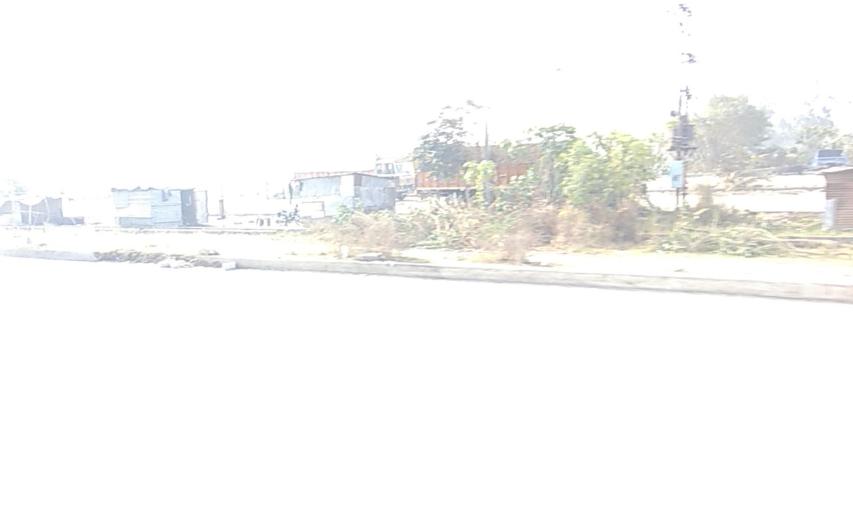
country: IN
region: Punjab
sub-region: Pathankot
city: Pathankot
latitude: 32.2572
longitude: 75.6369
